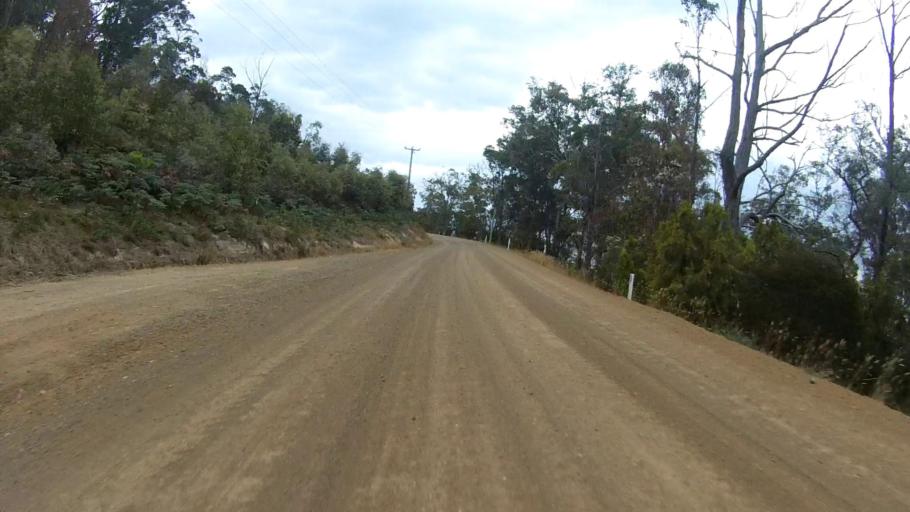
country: AU
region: Tasmania
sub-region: Huon Valley
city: Cygnet
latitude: -43.2202
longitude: 147.0922
